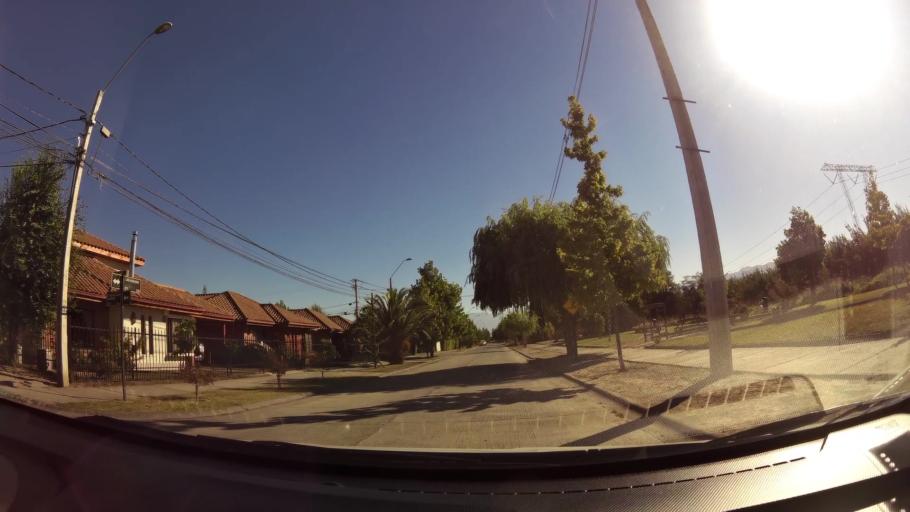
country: CL
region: O'Higgins
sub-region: Provincia de Cachapoal
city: Rancagua
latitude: -34.1954
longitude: -70.7184
